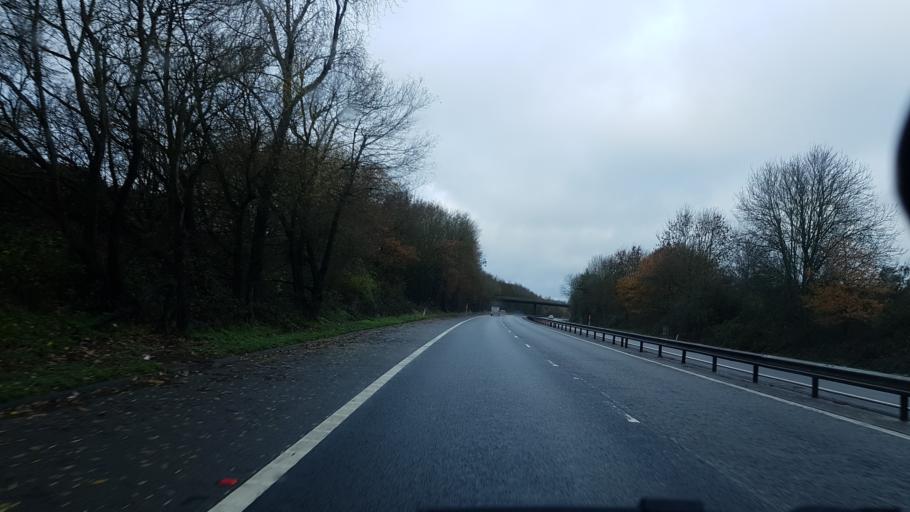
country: GB
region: England
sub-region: Bracknell Forest
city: Binfield
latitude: 51.4164
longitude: -0.8058
